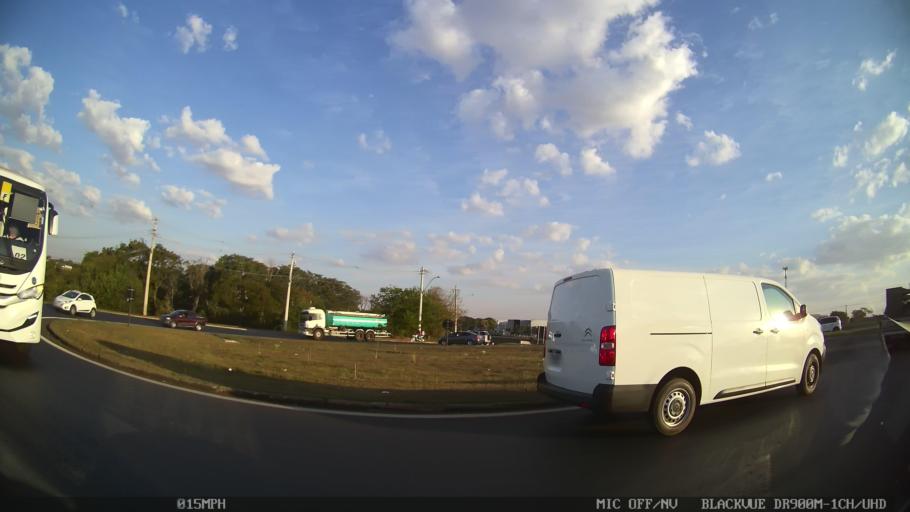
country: BR
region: Sao Paulo
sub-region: Ribeirao Preto
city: Ribeirao Preto
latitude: -21.1498
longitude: -47.7570
